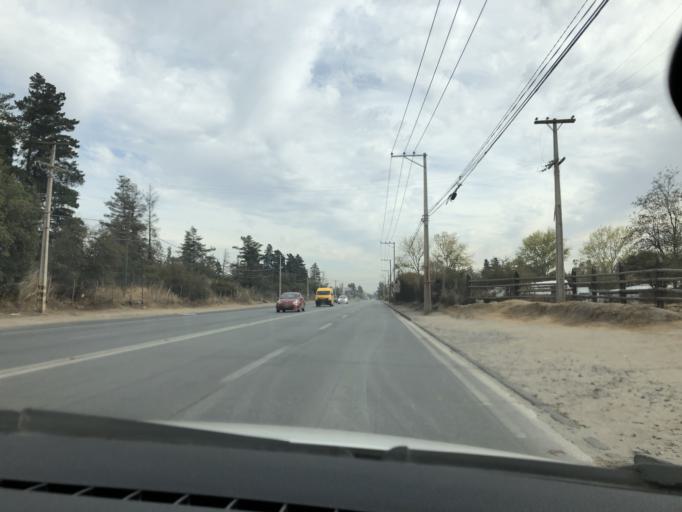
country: CL
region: Santiago Metropolitan
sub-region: Provincia de Cordillera
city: Puente Alto
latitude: -33.5979
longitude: -70.5126
